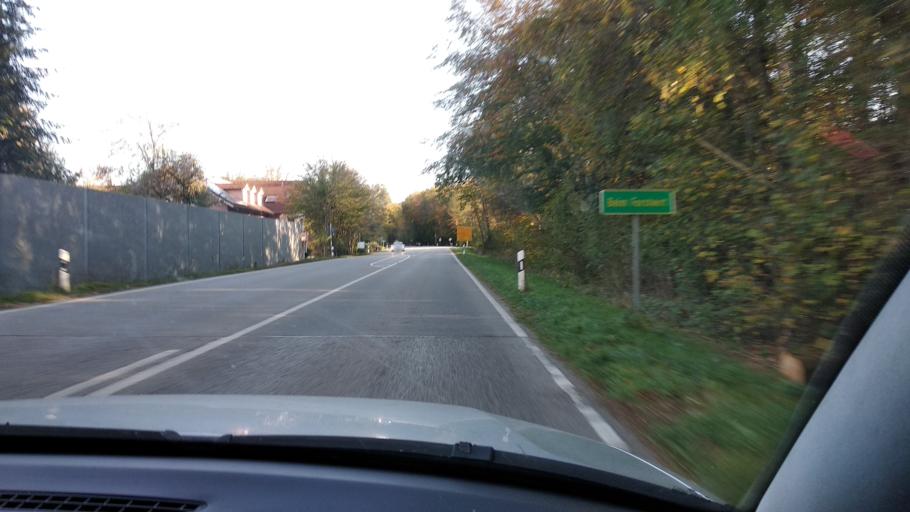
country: DE
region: Bavaria
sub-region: Upper Bavaria
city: Grasbrunn
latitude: 48.0504
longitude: 11.7624
